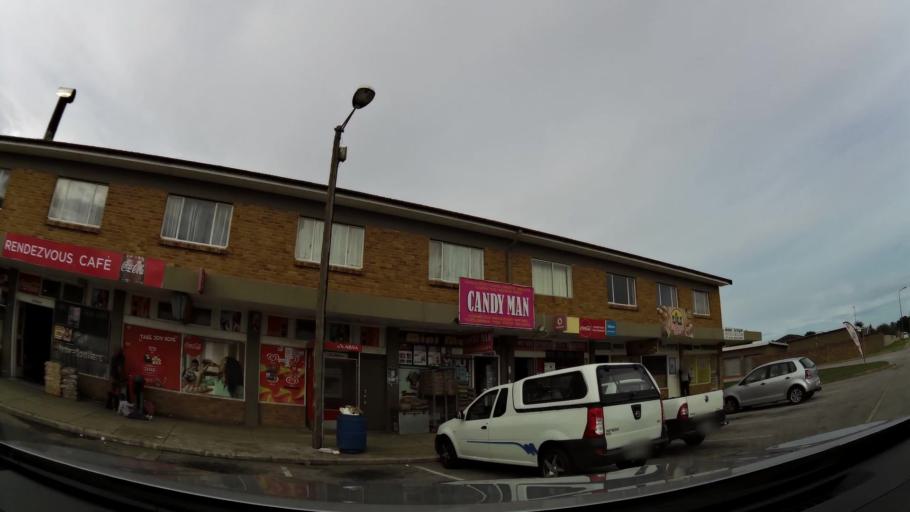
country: ZA
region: Eastern Cape
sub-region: Nelson Mandela Bay Metropolitan Municipality
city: Port Elizabeth
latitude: -33.9417
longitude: 25.4993
